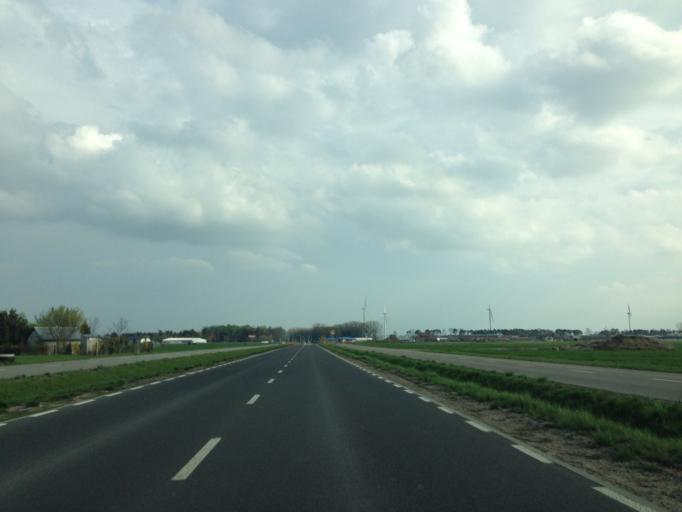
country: PL
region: Masovian Voivodeship
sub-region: Powiat zurominski
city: Zuromin
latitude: 53.0685
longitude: 19.8913
